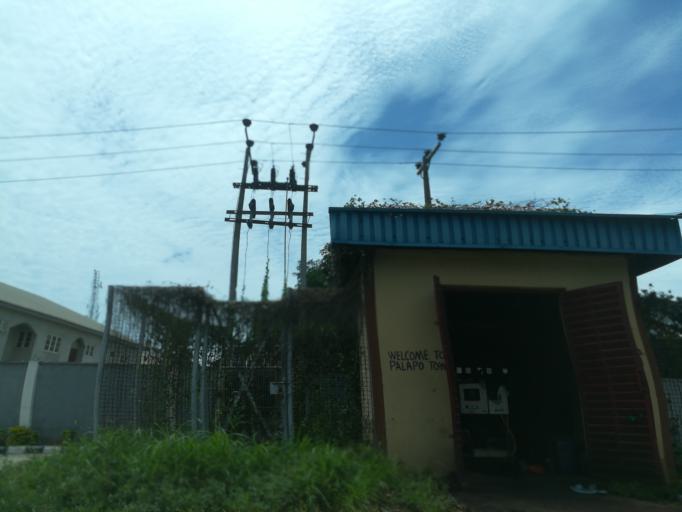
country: NG
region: Lagos
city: Ebute Ikorodu
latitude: 6.5884
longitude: 3.4924
